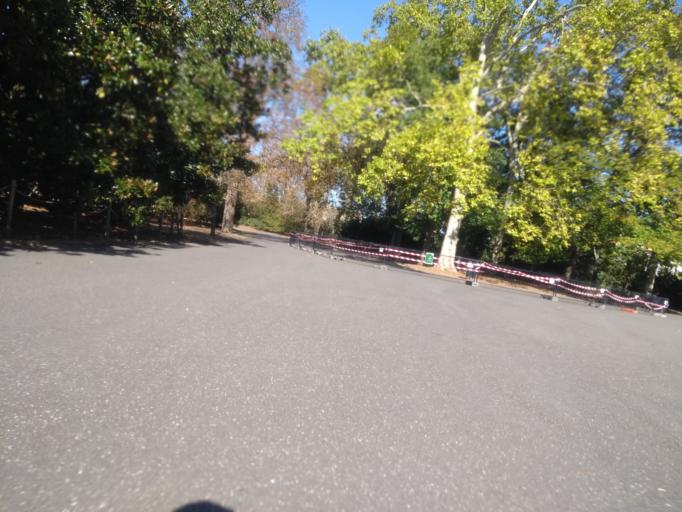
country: FR
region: Aquitaine
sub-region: Departement de la Gironde
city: Le Bouscat
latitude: 44.8536
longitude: -0.5996
